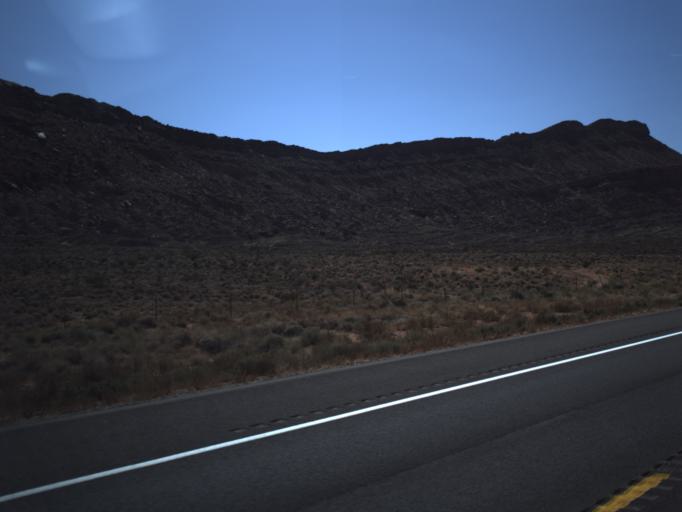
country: US
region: Utah
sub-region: Washington County
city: Washington
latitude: 37.0927
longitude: -113.4707
